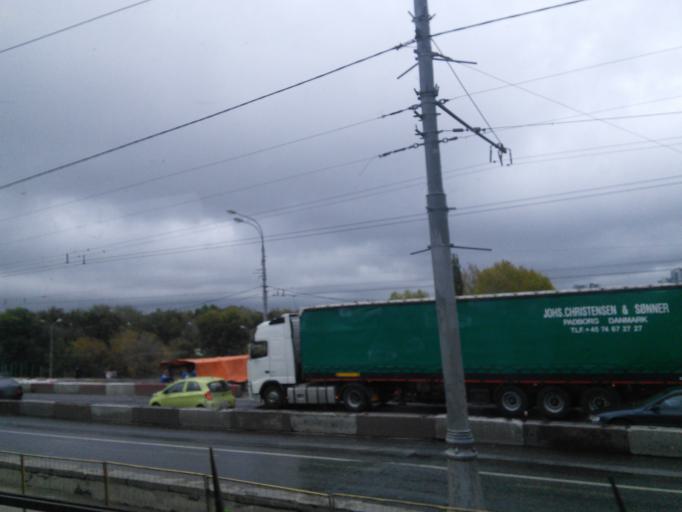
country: RU
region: Moskovskaya
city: Kozhukhovo
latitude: 55.6885
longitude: 37.6654
